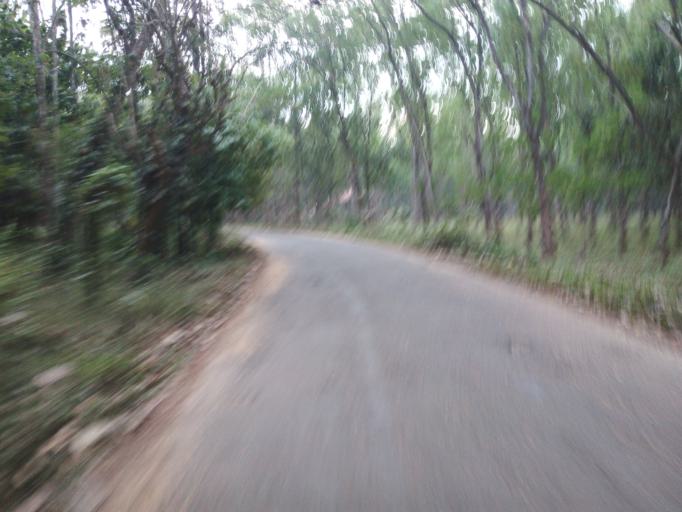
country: IN
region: Kerala
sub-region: Kottayam
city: Palackattumala
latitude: 9.8696
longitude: 76.6476
